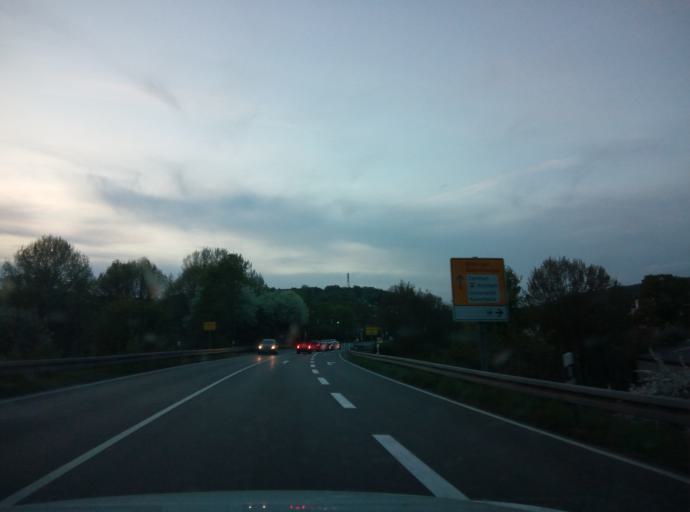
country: DE
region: Baden-Wuerttemberg
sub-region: Tuebingen Region
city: Tuebingen
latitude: 48.5262
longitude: 9.0783
